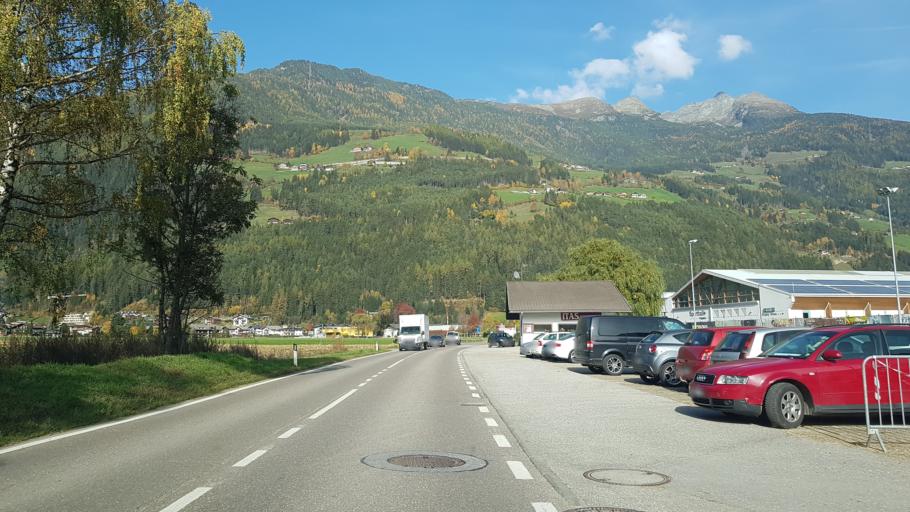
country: IT
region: Trentino-Alto Adige
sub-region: Bolzano
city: Campo Tures
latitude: 46.9104
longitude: 11.9603
